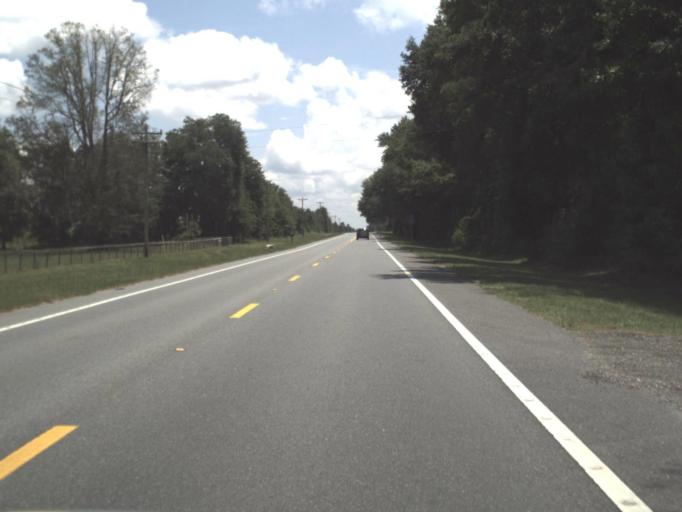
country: US
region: Florida
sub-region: Union County
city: Lake Butler
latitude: 30.0041
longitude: -82.4944
